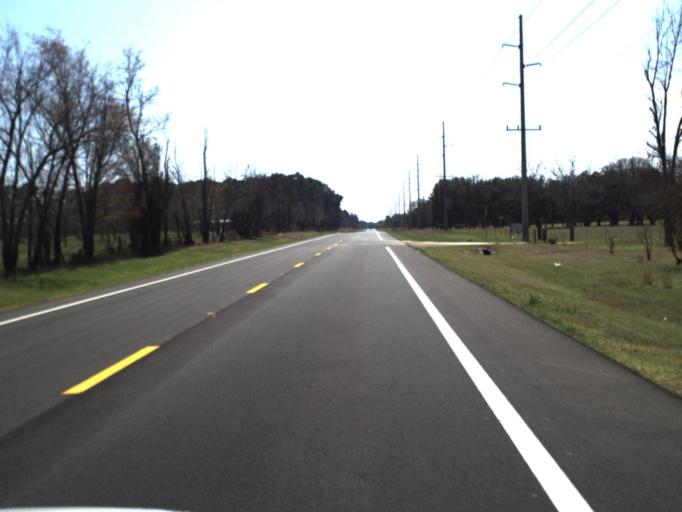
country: US
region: Florida
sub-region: Jackson County
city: Sneads
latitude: 30.7557
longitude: -85.0194
